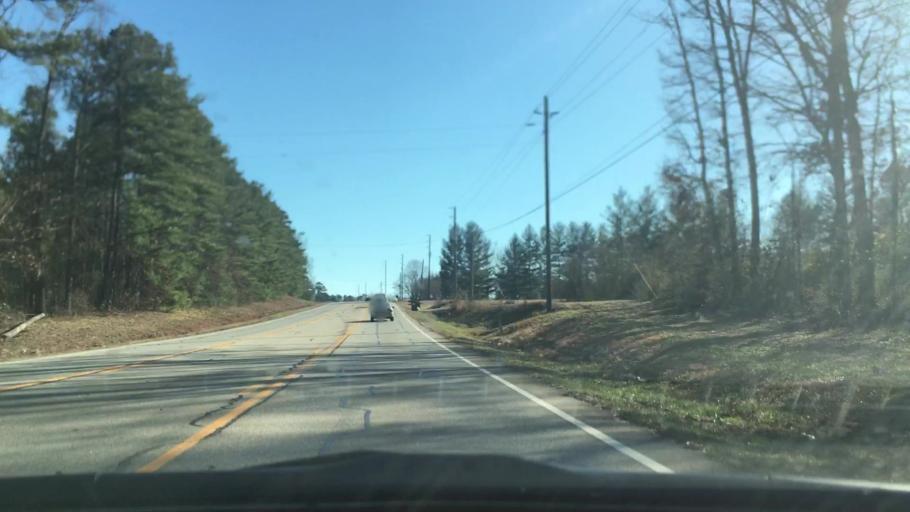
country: US
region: Georgia
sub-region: Henry County
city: McDonough
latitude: 33.5158
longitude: -84.1389
